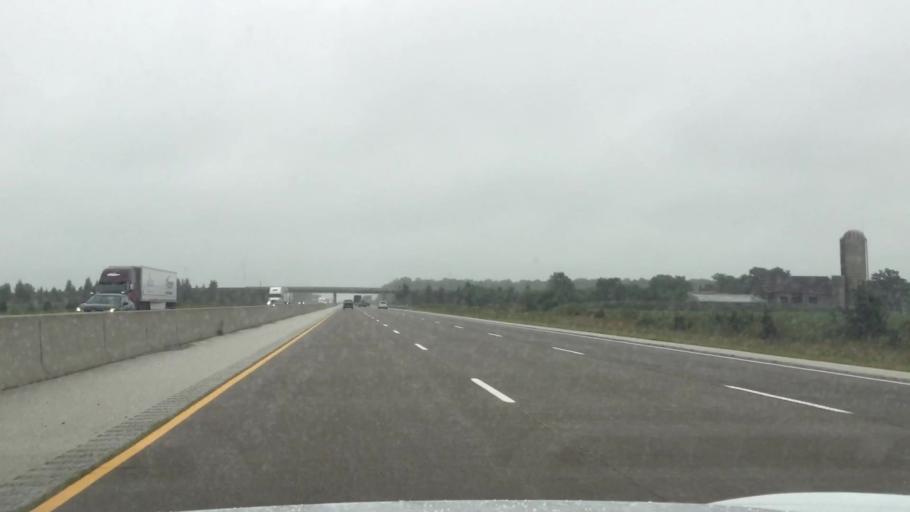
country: US
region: Michigan
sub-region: Wayne County
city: Grosse Pointe
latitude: 42.2378
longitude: -82.7589
